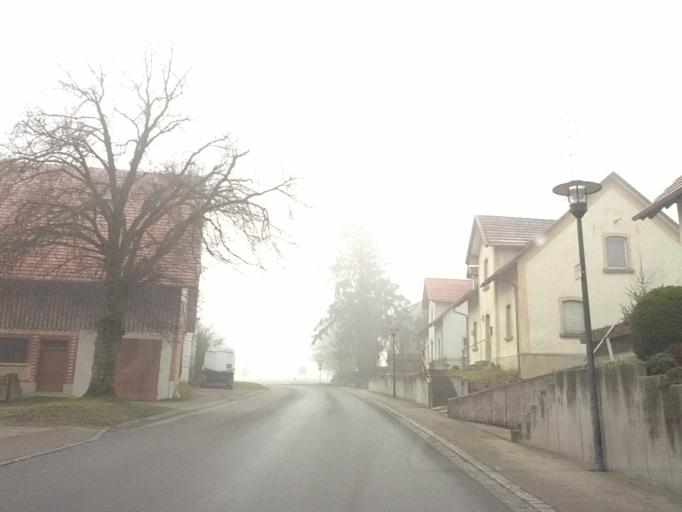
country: DE
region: Baden-Wuerttemberg
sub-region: Tuebingen Region
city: Steinhausen an der Rottum
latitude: 47.9728
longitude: 9.9395
